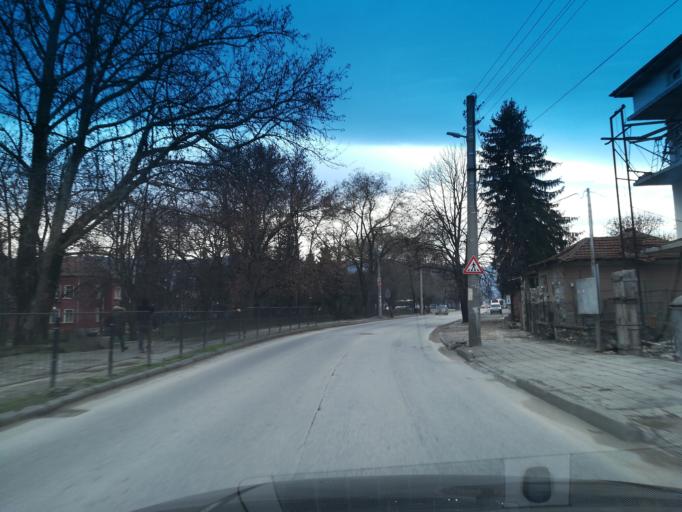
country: BG
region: Plovdiv
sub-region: Obshtina Plovdiv
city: Plovdiv
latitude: 42.1017
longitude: 24.7033
